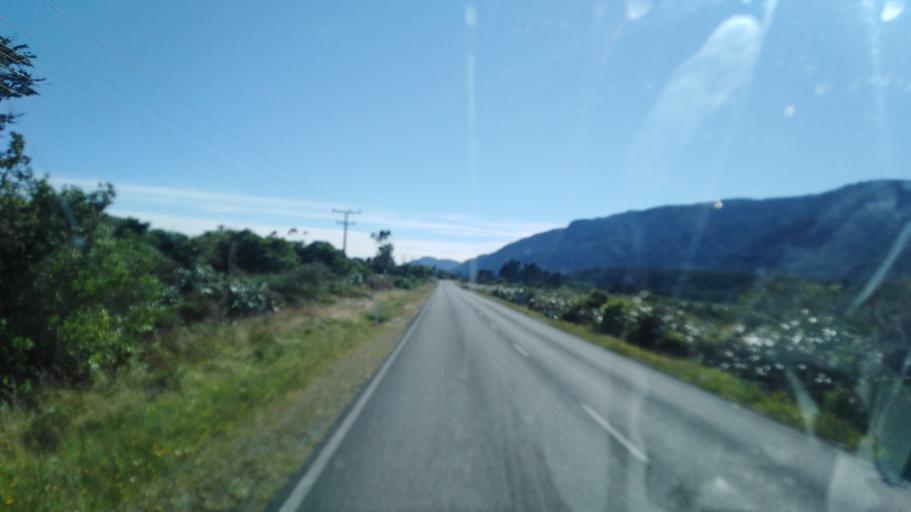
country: NZ
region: West Coast
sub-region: Buller District
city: Westport
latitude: -41.6816
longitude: 171.7915
